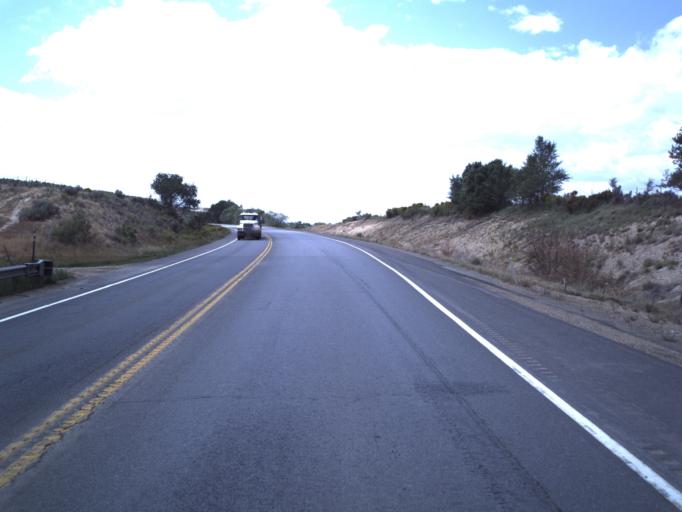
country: US
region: Utah
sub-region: Duchesne County
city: Duchesne
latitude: 40.1695
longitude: -110.3038
